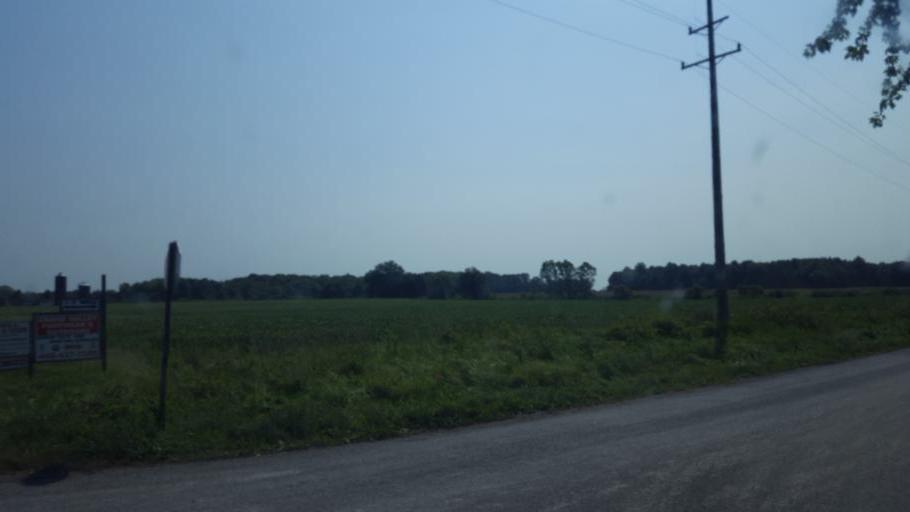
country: US
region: Ohio
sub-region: Ashtabula County
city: Orwell
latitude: 41.5350
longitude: -80.8847
